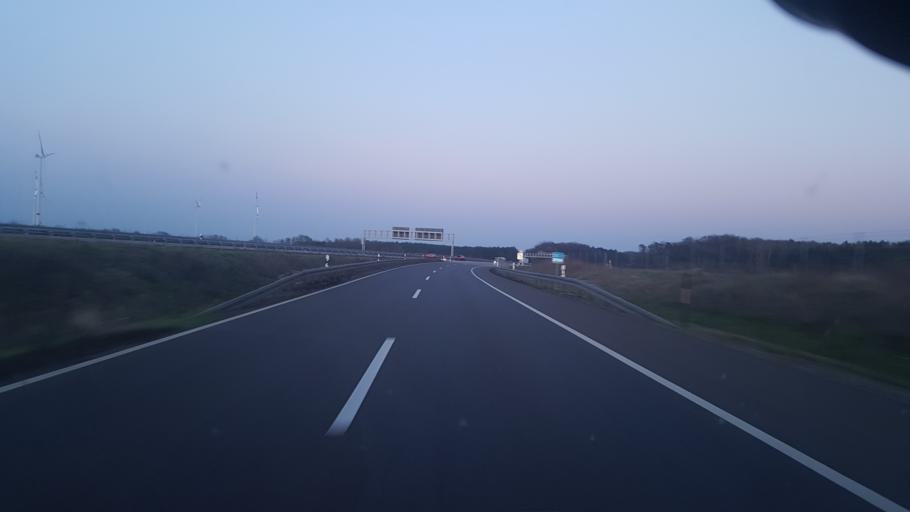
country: DE
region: Brandenburg
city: Ahrensfelde
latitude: 52.6112
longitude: 13.5728
